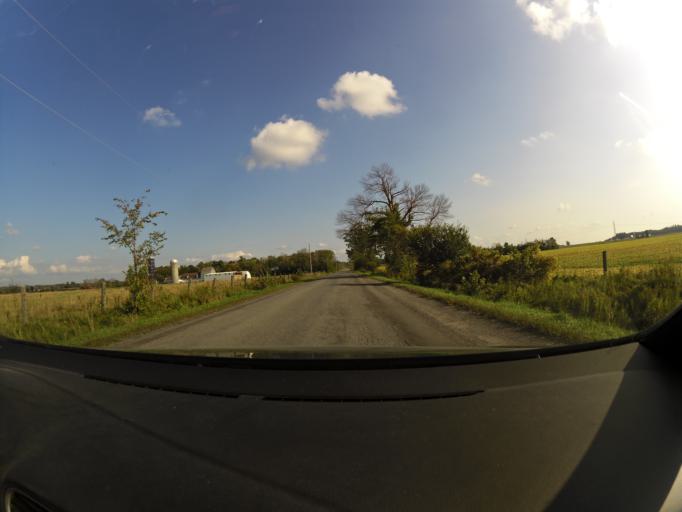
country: CA
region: Ontario
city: Arnprior
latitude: 45.4156
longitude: -76.2199
